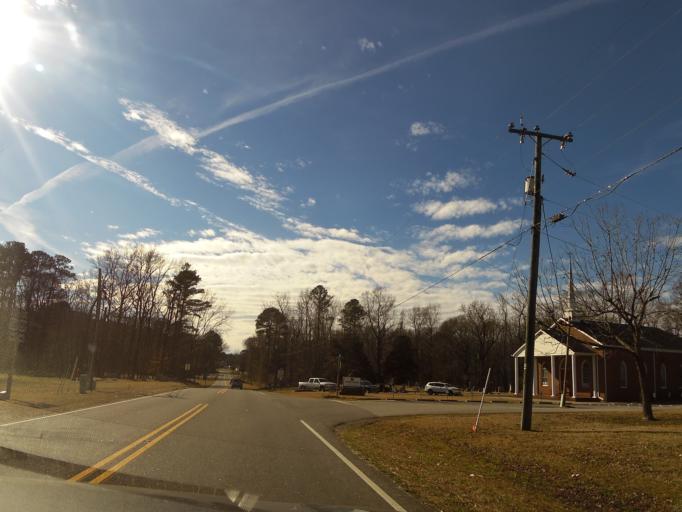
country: US
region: Virginia
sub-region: Isle of Wight County
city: Windsor
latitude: 36.7765
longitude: -76.8425
